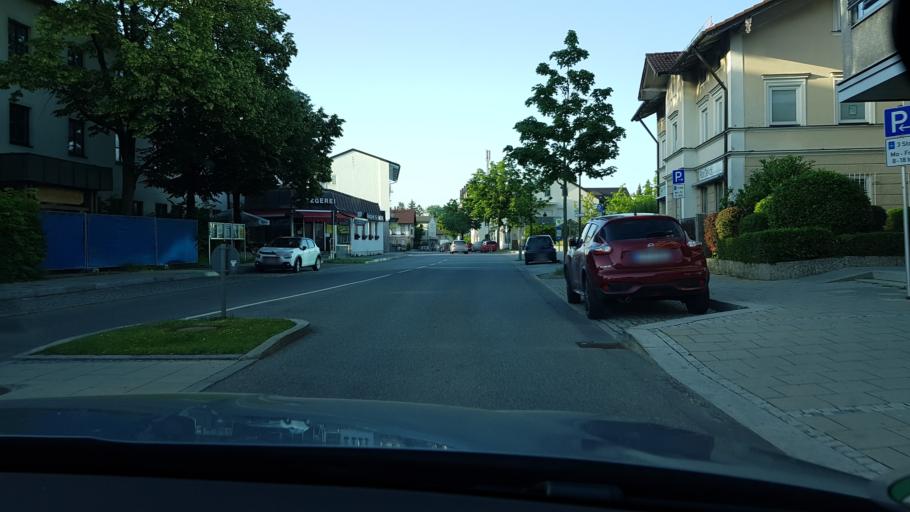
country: DE
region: Bavaria
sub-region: Upper Bavaria
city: Unterfoehring
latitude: 48.1924
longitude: 11.6406
